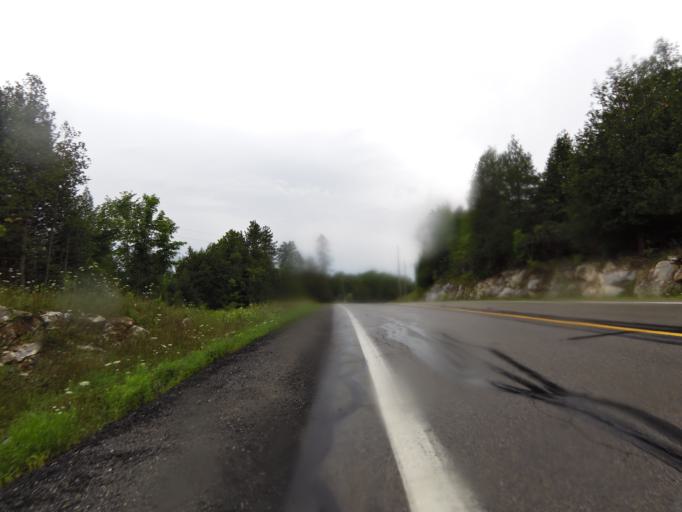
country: CA
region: Ontario
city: Perth
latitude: 44.9822
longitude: -76.4001
